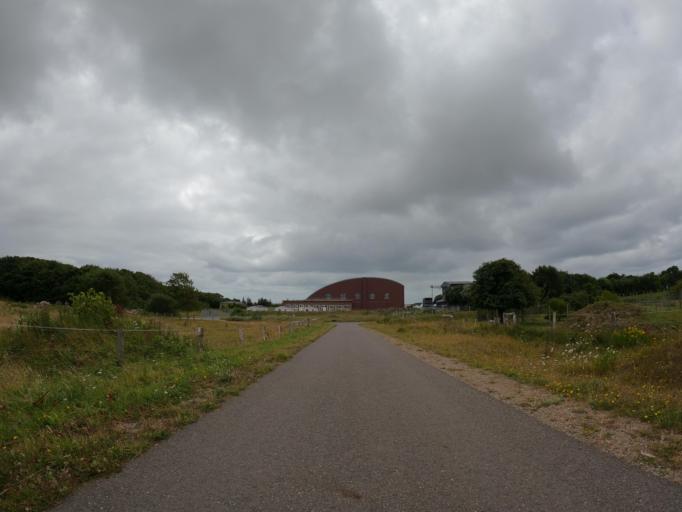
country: DE
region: Schleswig-Holstein
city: Tinnum
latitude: 54.9200
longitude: 8.3475
